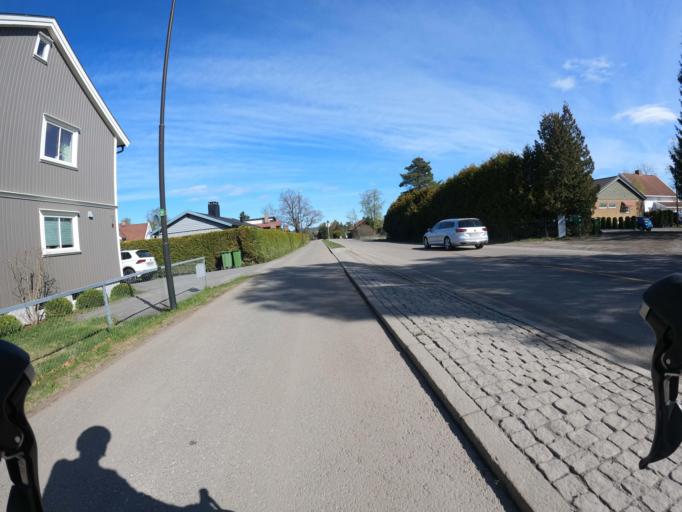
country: NO
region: Akershus
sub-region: Skedsmo
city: Lillestrom
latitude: 59.9639
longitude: 11.0087
